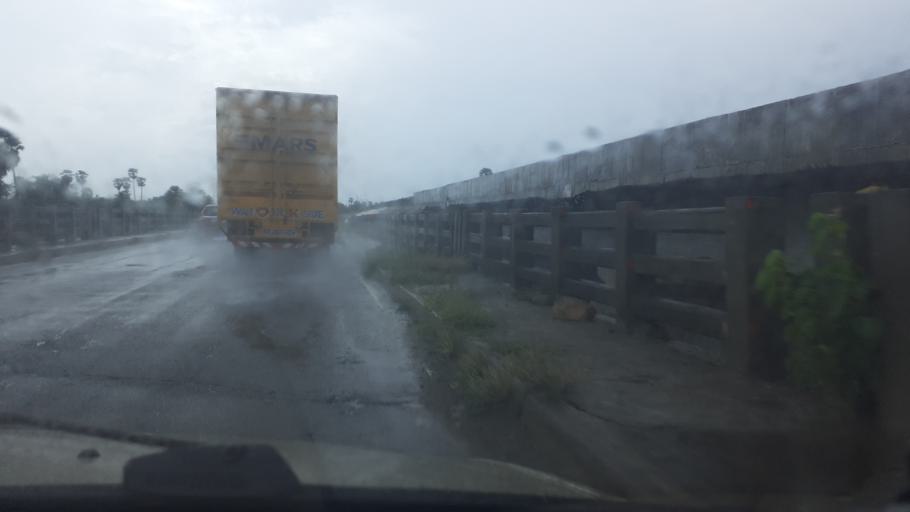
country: IN
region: Tamil Nadu
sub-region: Thoothukkudi
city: Kayattar
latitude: 8.9275
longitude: 77.7674
